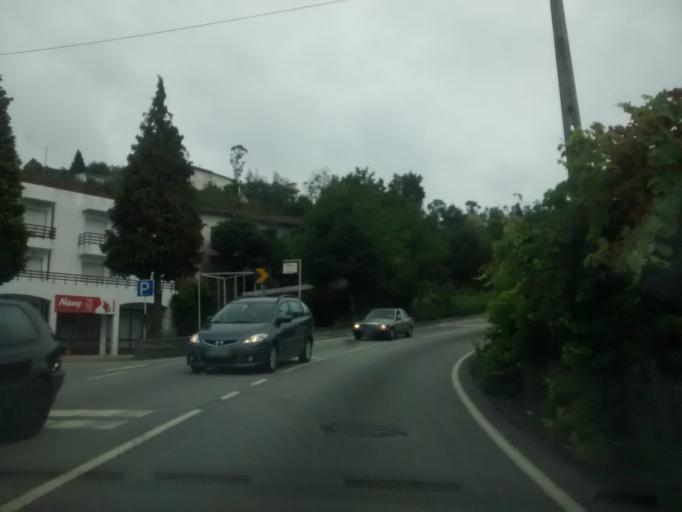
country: PT
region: Braga
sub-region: Braga
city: Oliveira
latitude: 41.4671
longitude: -8.4891
